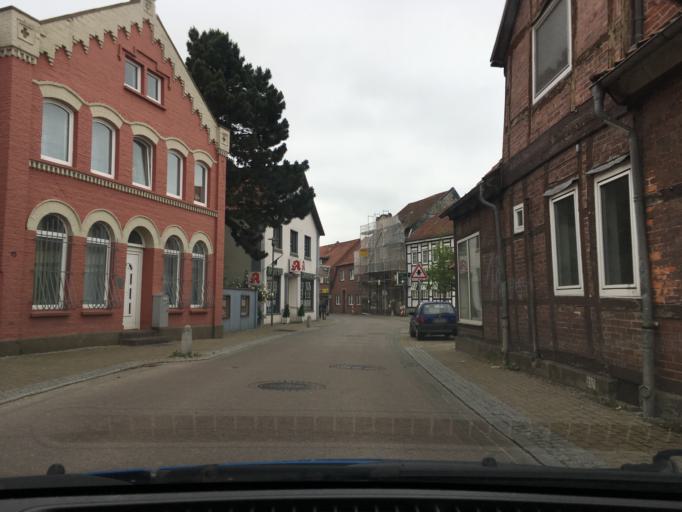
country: DE
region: Lower Saxony
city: Dahlenburg
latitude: 53.1864
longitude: 10.7435
